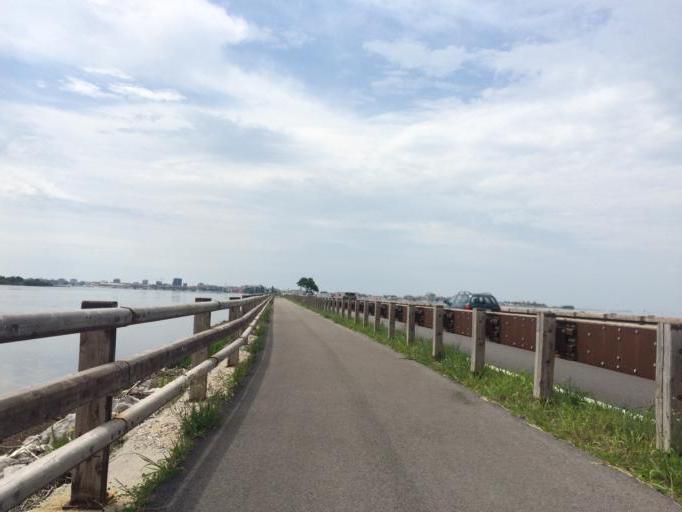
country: IT
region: Friuli Venezia Giulia
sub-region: Provincia di Gorizia
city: Grado
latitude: 45.6991
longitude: 13.3835
